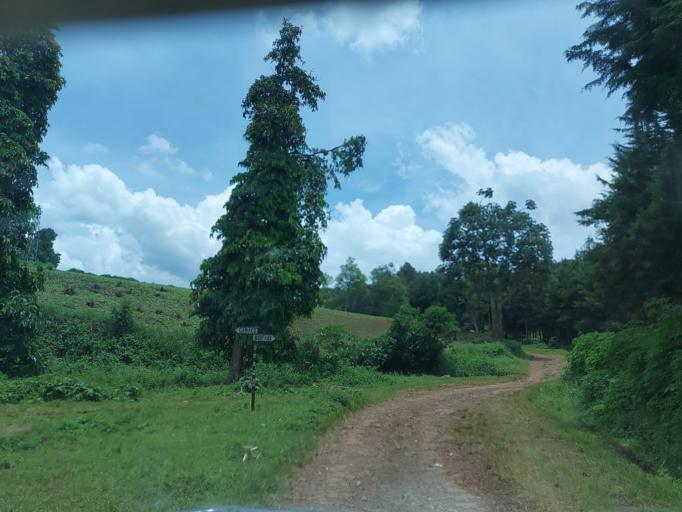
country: CD
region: South Kivu
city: Kabare
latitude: -2.3363
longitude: 28.7842
